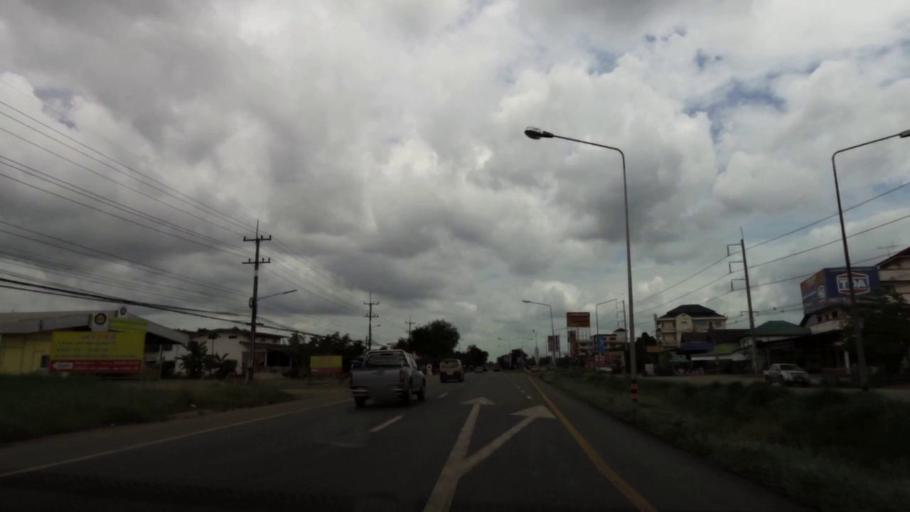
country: TH
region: Rayong
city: Klaeng
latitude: 12.7817
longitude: 101.6939
